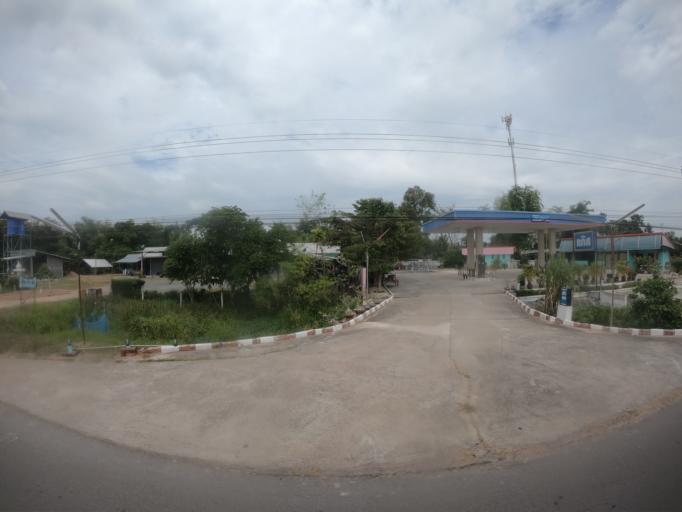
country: TH
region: Roi Et
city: Changhan
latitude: 16.0964
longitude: 103.5363
